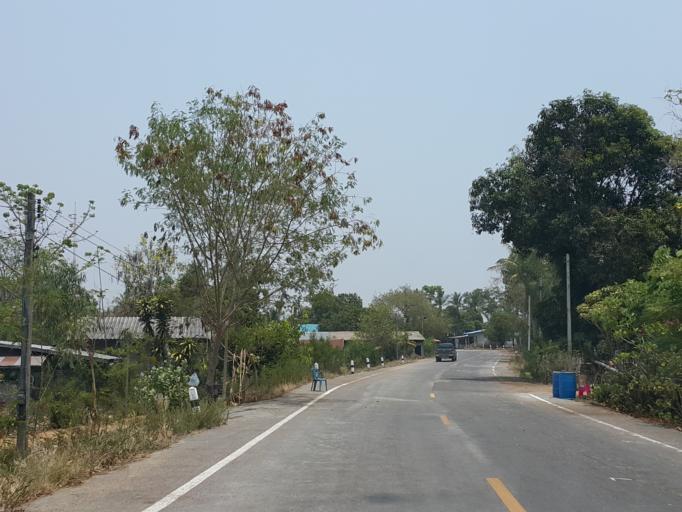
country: TH
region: Kamphaeng Phet
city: Pang Sila Thong
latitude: 16.0549
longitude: 99.3511
